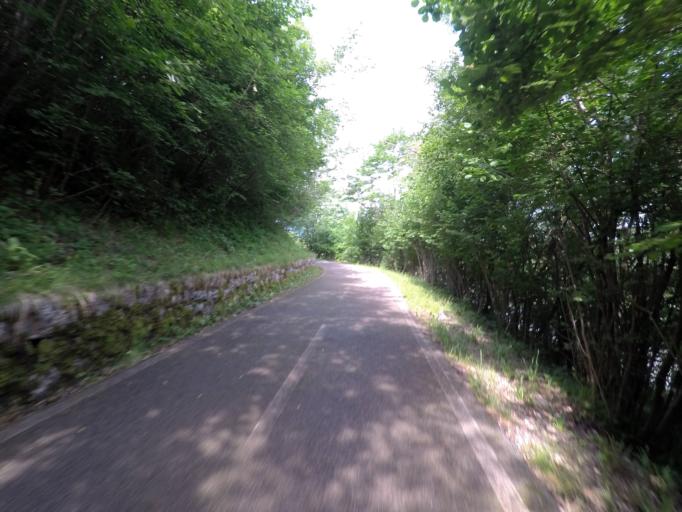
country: IT
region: Friuli Venezia Giulia
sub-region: Provincia di Udine
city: Amaro
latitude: 46.3613
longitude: 13.0832
